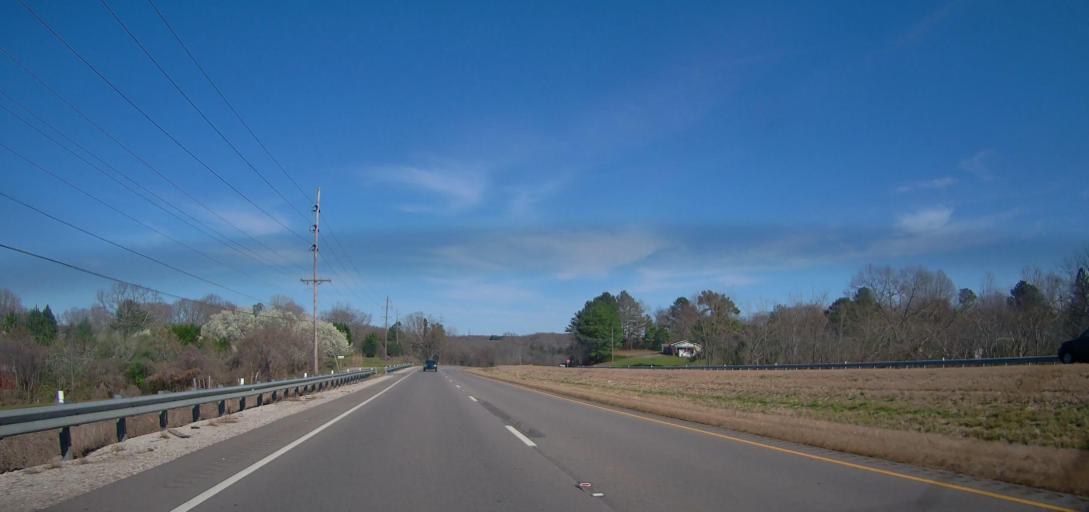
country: US
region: Alabama
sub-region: Lauderdale County
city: Killen
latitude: 34.8598
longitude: -87.4225
